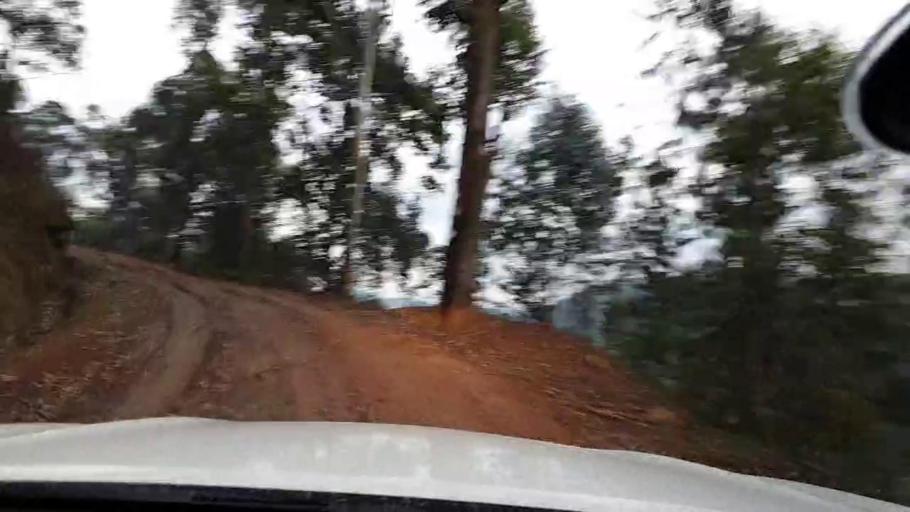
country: RW
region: Western Province
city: Cyangugu
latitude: -2.4110
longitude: 29.1868
